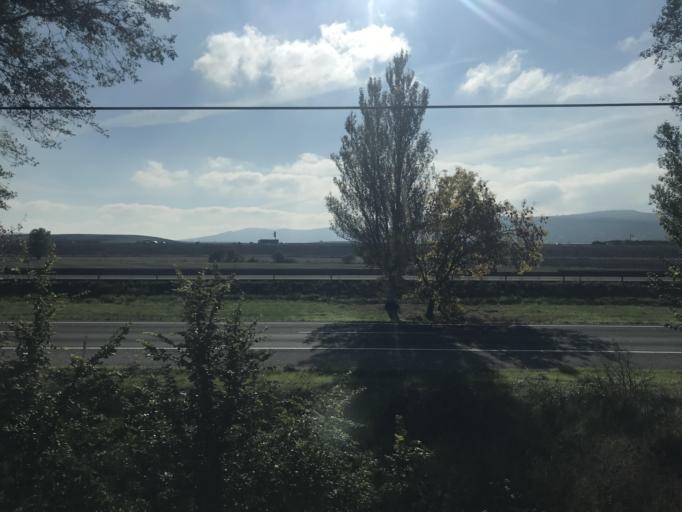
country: ES
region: Basque Country
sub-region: Provincia de Alava
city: Arminon
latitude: 42.7564
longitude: -2.8346
